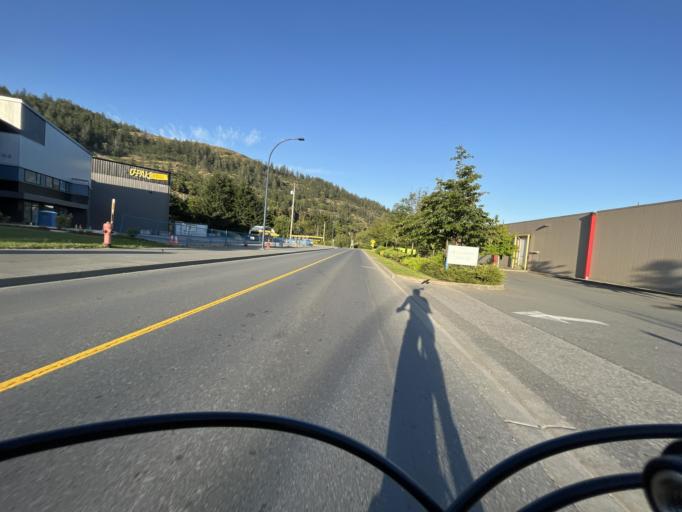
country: CA
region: British Columbia
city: Langford
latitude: 48.4579
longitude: -123.5422
